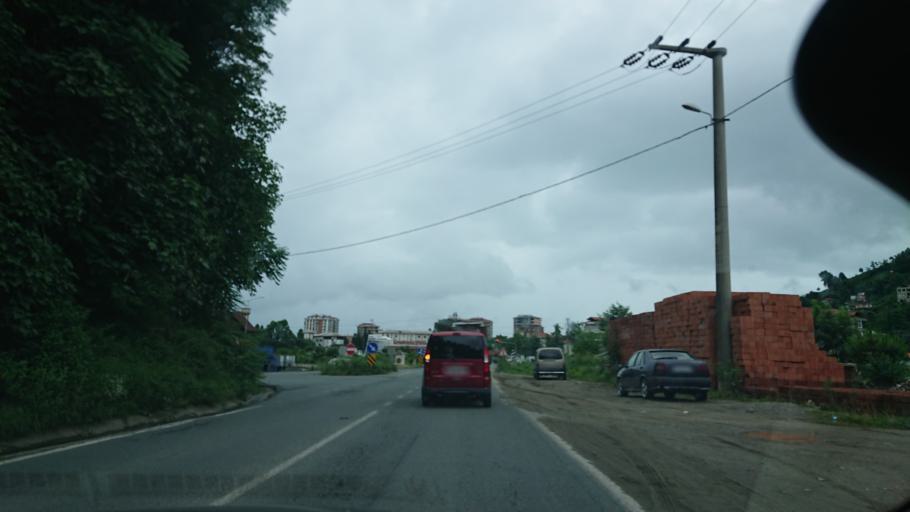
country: TR
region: Rize
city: Gundogdu
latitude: 41.0366
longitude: 40.5791
